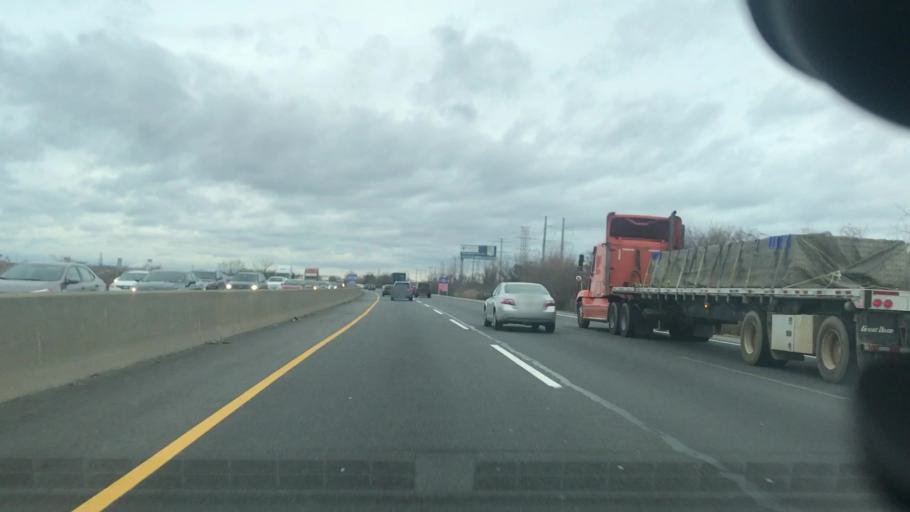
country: US
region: New Jersey
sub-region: Hudson County
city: North Bergen
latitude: 40.8075
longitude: -74.0313
